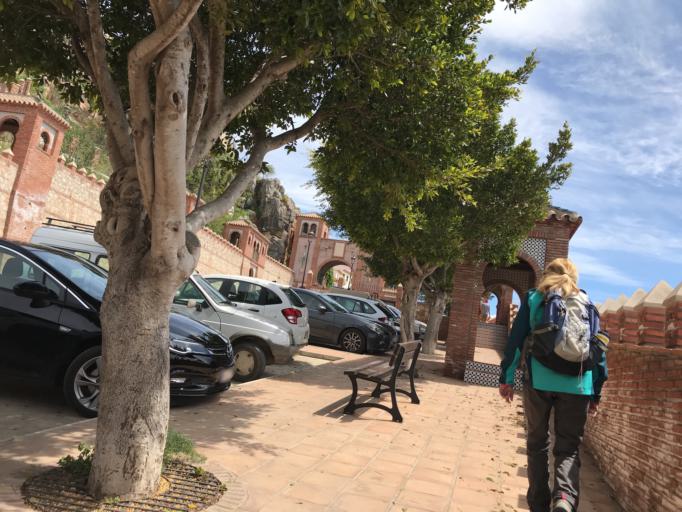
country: ES
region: Andalusia
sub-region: Provincia de Malaga
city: Comares
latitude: 36.8477
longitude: -4.2484
